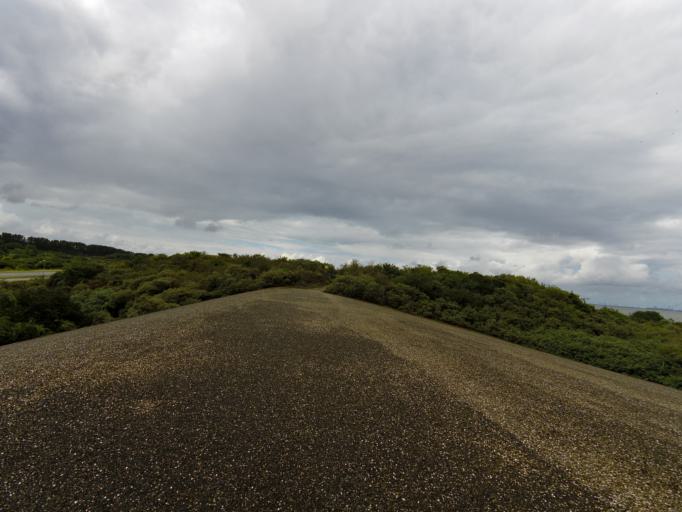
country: NL
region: South Holland
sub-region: Gemeente Goeree-Overflakkee
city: Goedereede
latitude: 51.8283
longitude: 4.0245
